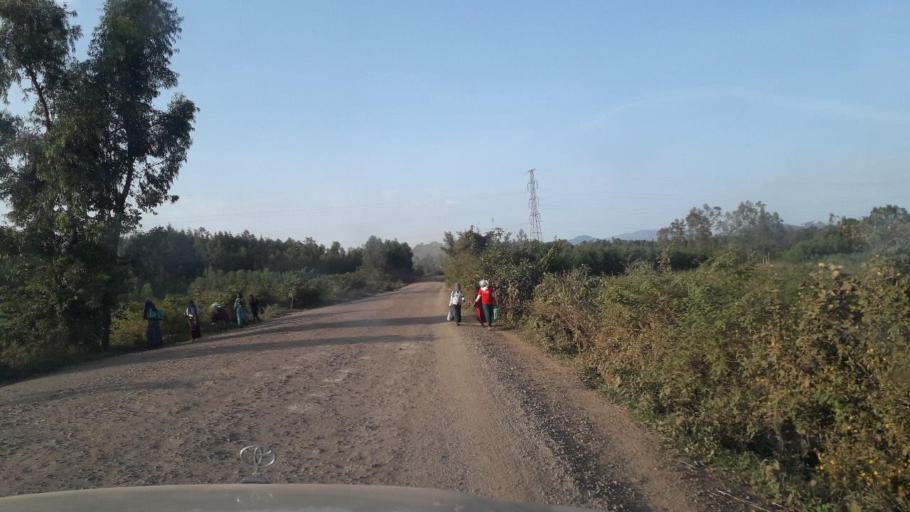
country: ET
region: Oromiya
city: Jima
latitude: 7.6158
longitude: 36.8340
